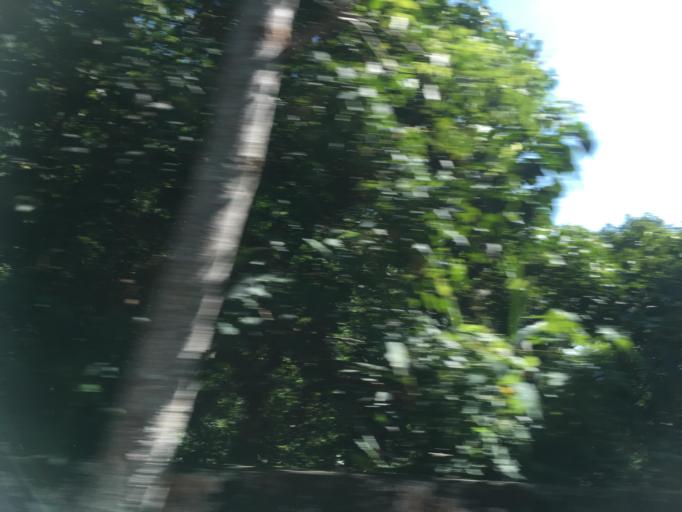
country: TW
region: Taiwan
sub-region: Yilan
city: Yilan
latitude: 24.4385
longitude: 121.7529
